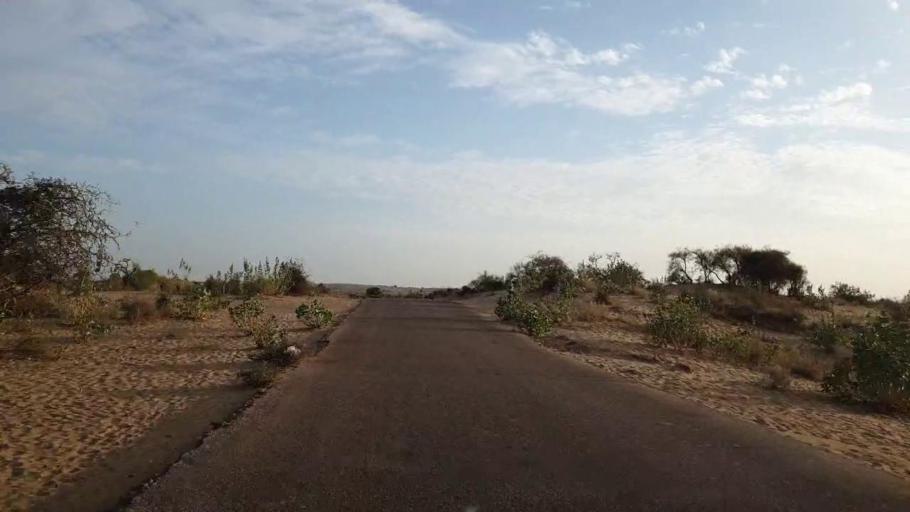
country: PK
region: Sindh
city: Nabisar
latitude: 25.1001
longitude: 69.9929
